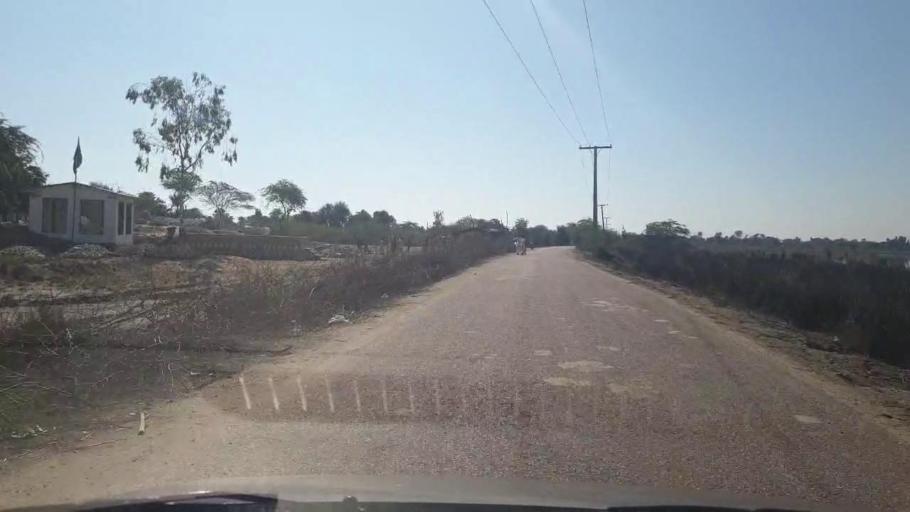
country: PK
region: Sindh
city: Bozdar
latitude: 27.1323
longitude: 68.6418
